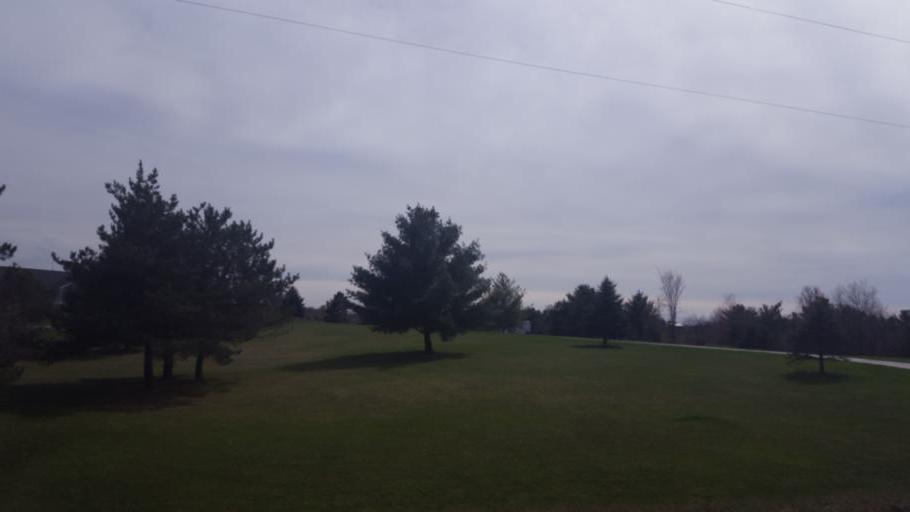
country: US
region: Michigan
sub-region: Gladwin County
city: Gladwin
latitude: 43.9879
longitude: -84.5417
